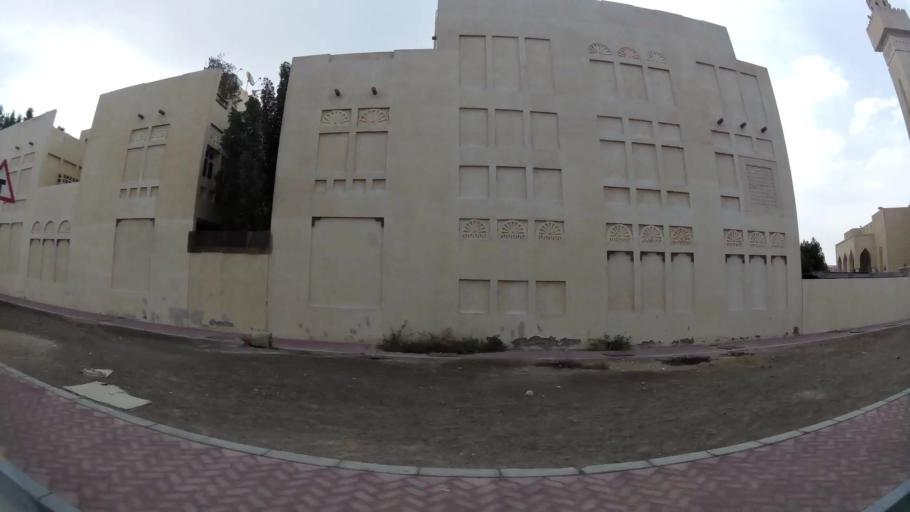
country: AE
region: Abu Dhabi
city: Abu Dhabi
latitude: 24.4768
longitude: 54.3856
